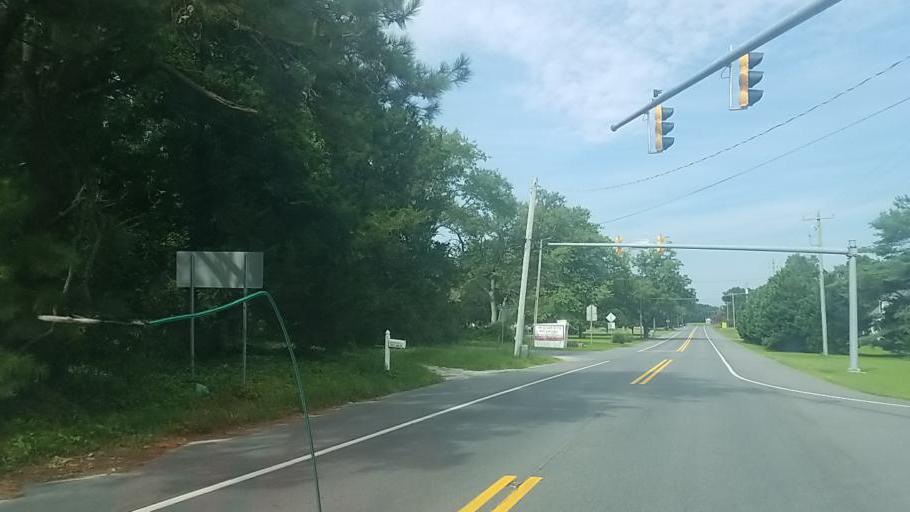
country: US
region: Delaware
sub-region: Sussex County
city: Ocean View
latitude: 38.5480
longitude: -75.1504
